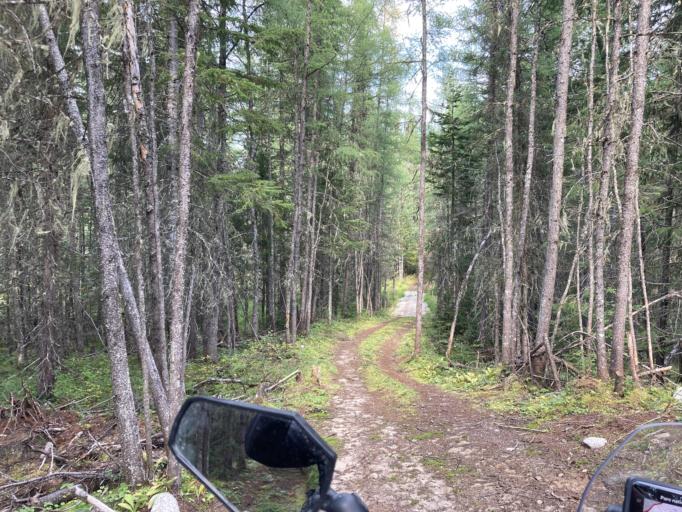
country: CA
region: Quebec
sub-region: Capitale-Nationale
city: Baie-Saint-Paul
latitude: 47.7029
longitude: -70.9530
